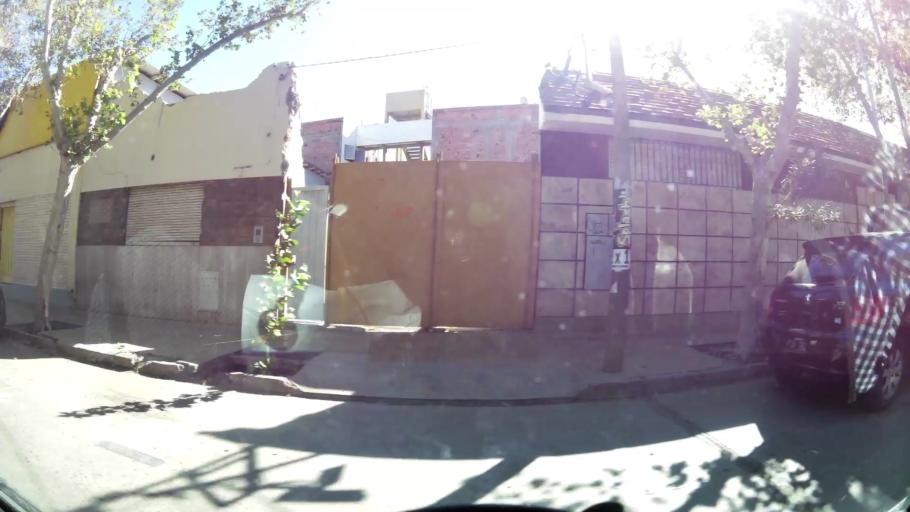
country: AR
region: San Juan
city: San Juan
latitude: -31.5366
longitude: -68.5351
